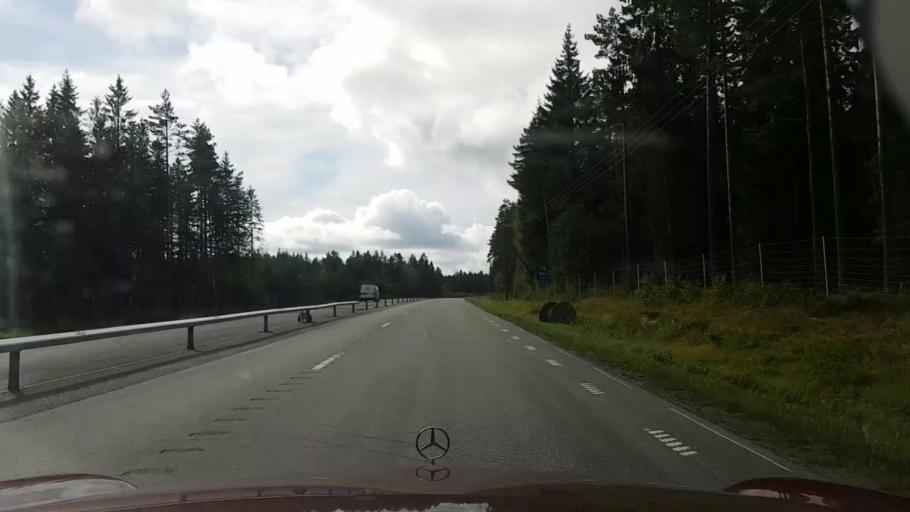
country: SE
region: OErebro
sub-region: Askersunds Kommun
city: Asbro
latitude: 58.9554
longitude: 15.0332
